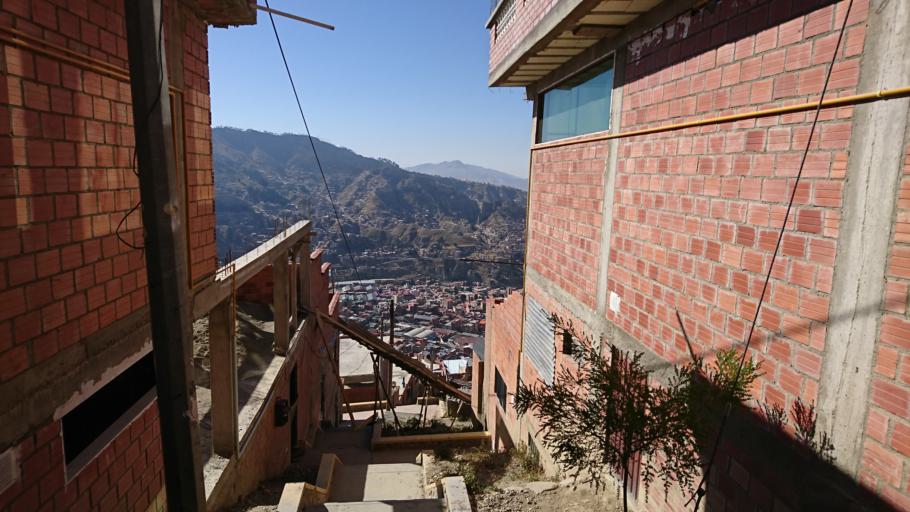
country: BO
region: La Paz
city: La Paz
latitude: -16.4710
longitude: -68.1254
